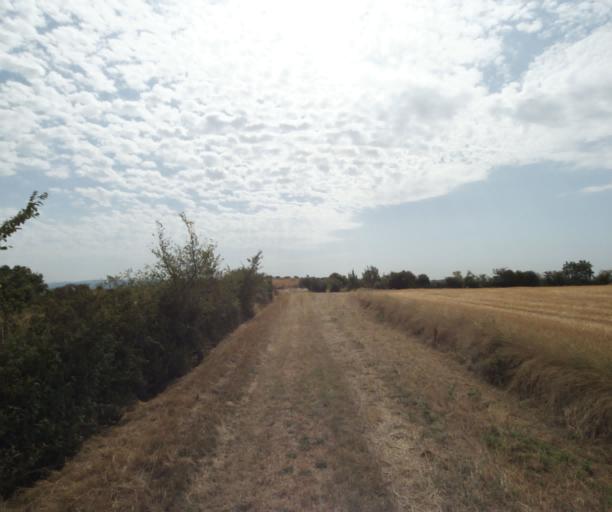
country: FR
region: Midi-Pyrenees
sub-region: Departement de la Haute-Garonne
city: Saint-Felix-Lauragais
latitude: 43.4469
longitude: 1.8992
